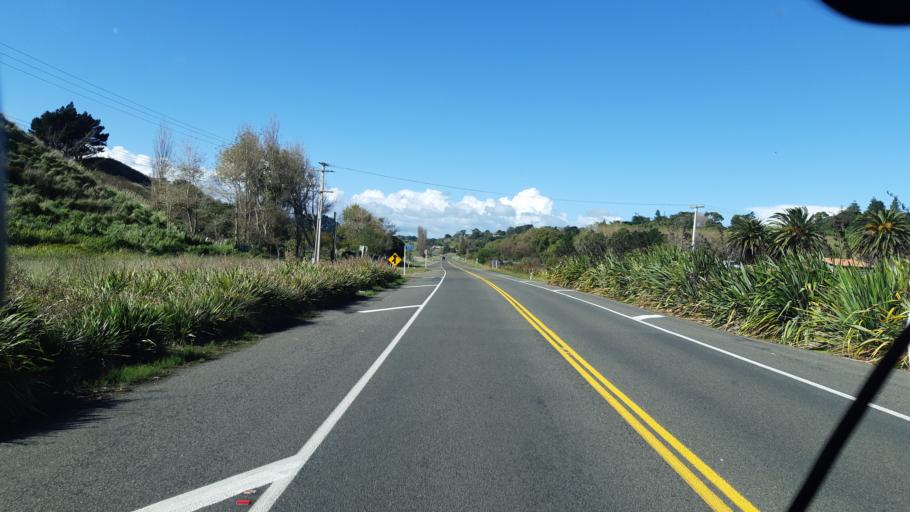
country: NZ
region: Manawatu-Wanganui
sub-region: Wanganui District
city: Wanganui
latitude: -39.9505
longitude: 175.0549
